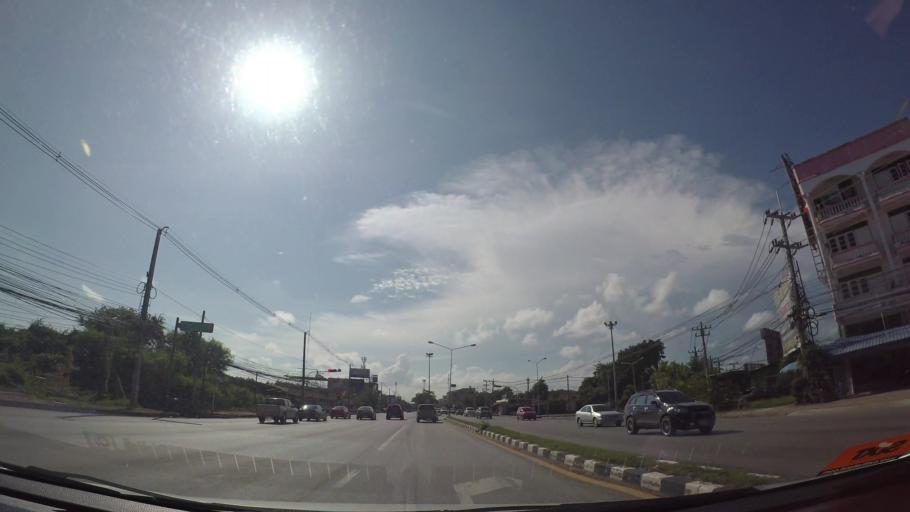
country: TH
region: Rayong
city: Rayong
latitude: 12.6697
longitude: 101.2943
